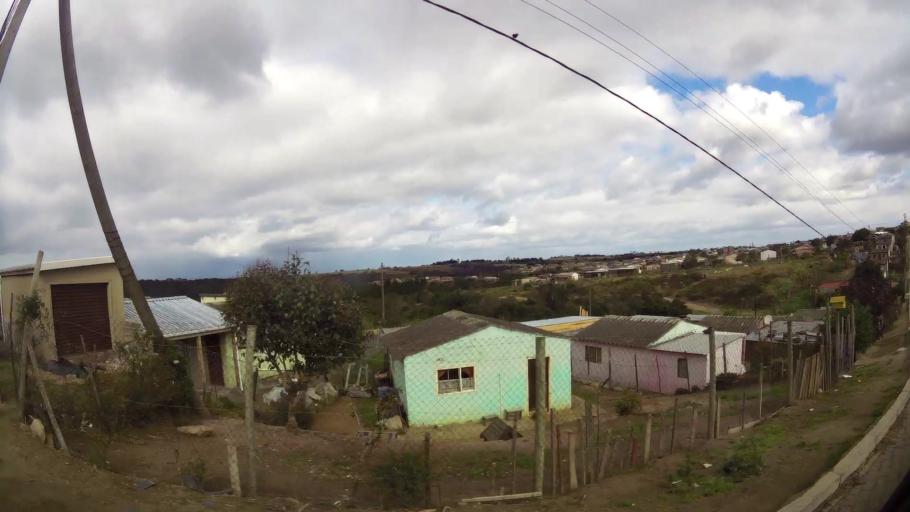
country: ZA
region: Western Cape
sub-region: Eden District Municipality
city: George
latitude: -34.0199
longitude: 22.4824
